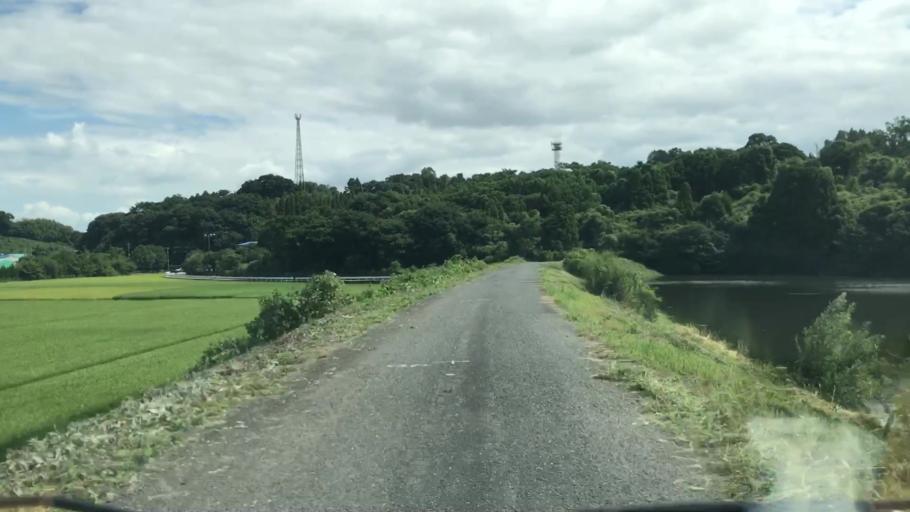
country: JP
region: Saga Prefecture
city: Saga-shi
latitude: 33.2323
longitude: 130.1731
